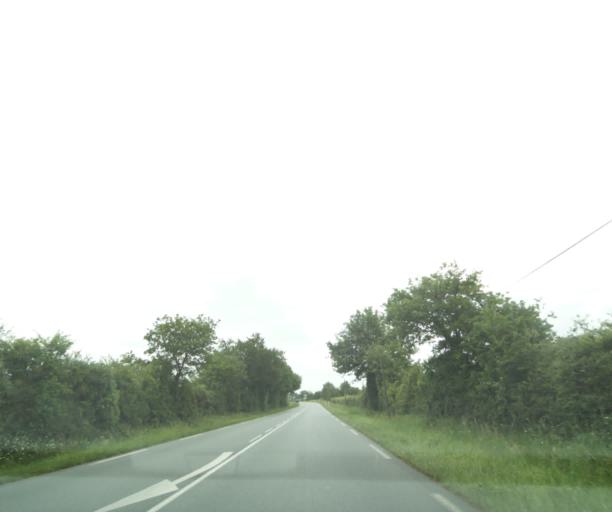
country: FR
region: Poitou-Charentes
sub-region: Departement des Deux-Sevres
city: Viennay
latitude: 46.7020
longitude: -0.2396
